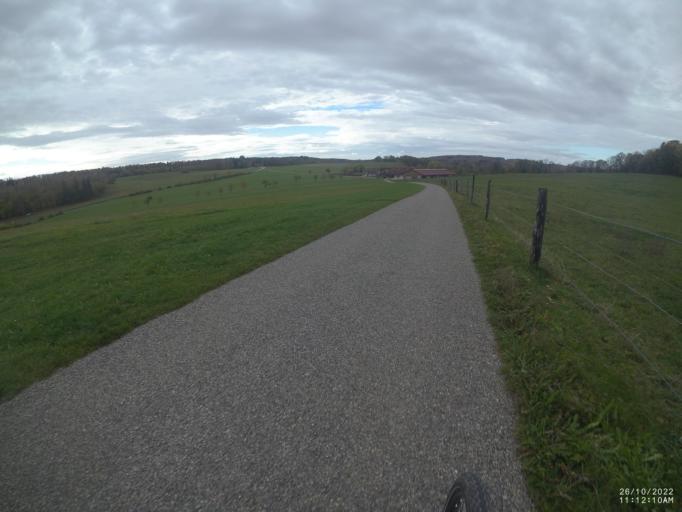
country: DE
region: Baden-Wuerttemberg
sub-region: Regierungsbezirk Stuttgart
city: Neidlingen
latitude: 48.5674
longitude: 9.5785
